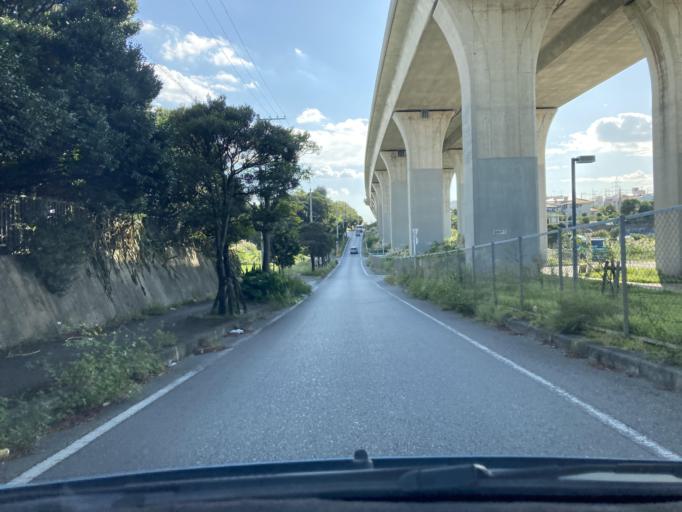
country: JP
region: Okinawa
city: Tomigusuku
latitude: 26.1927
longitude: 127.7394
